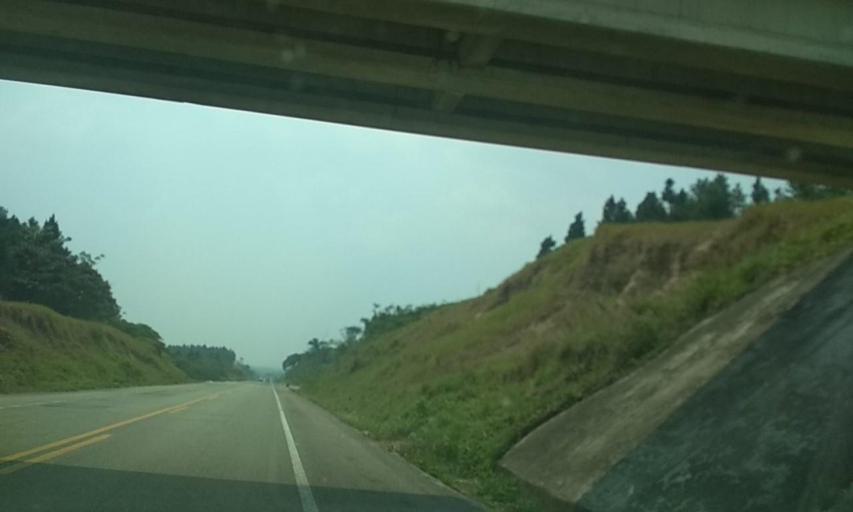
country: MX
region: Tabasco
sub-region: Huimanguillo
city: Francisco Rueda
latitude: 17.7498
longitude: -93.9940
